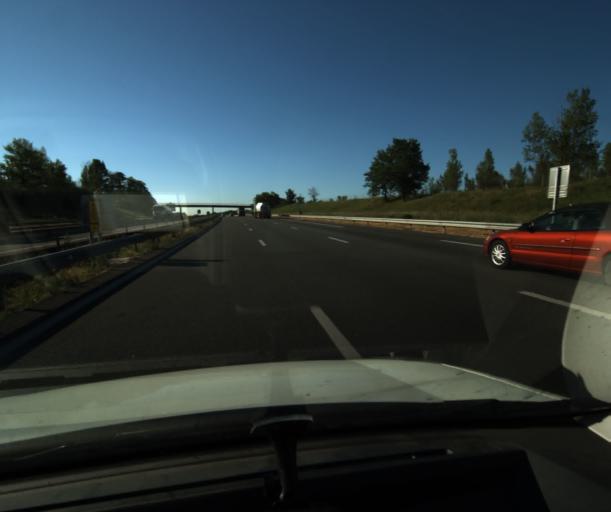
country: FR
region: Midi-Pyrenees
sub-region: Departement de la Haute-Garonne
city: Castelnau-d'Estretefonds
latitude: 43.7999
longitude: 1.3707
